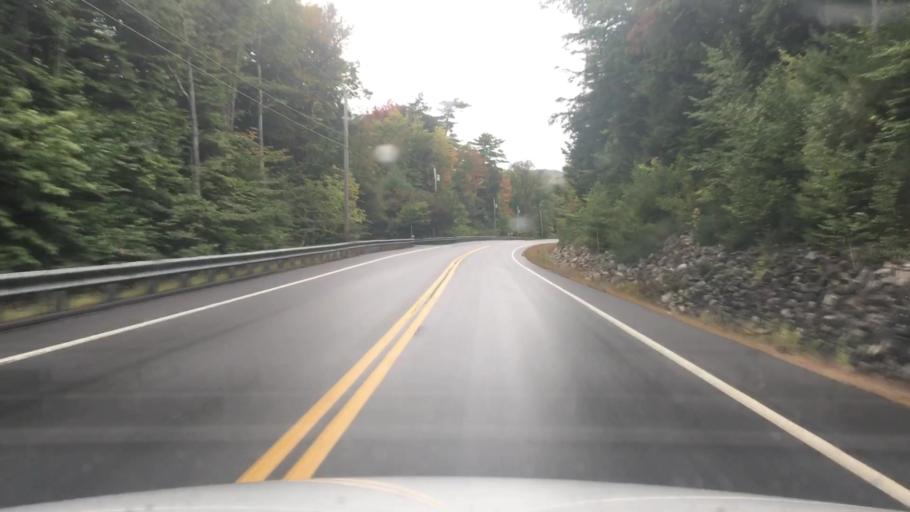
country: US
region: Maine
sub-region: Kennebec County
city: Rome
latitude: 44.5459
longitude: -69.8937
